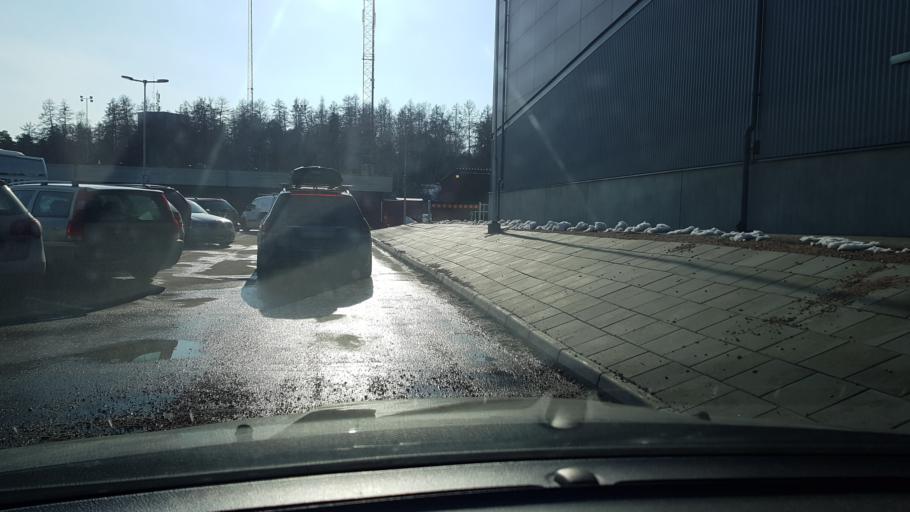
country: SE
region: Vaestmanland
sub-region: Sala Kommun
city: Sala
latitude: 59.9219
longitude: 16.5843
